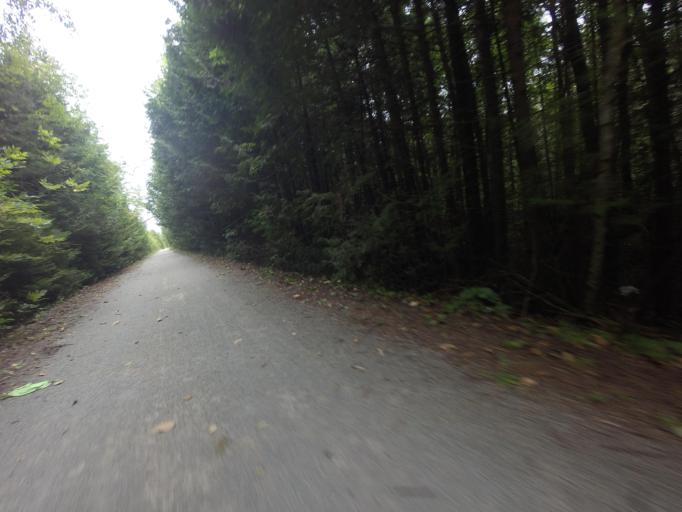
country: CA
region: Ontario
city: Uxbridge
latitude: 44.2609
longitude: -79.0271
